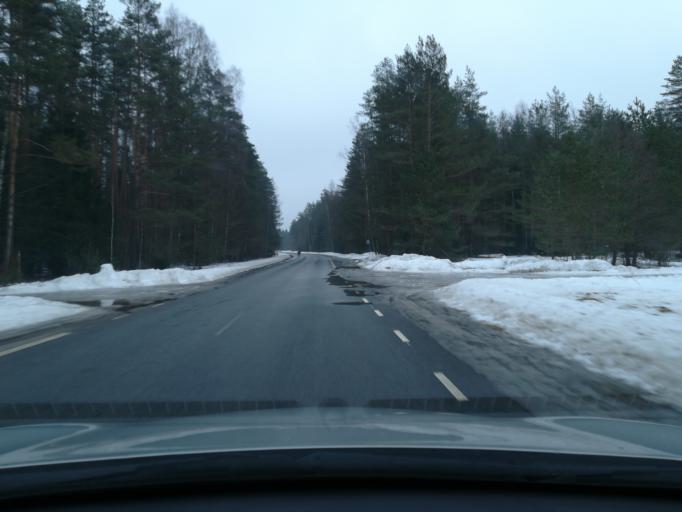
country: EE
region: Harju
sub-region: Loksa linn
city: Loksa
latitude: 59.4756
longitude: 25.6084
